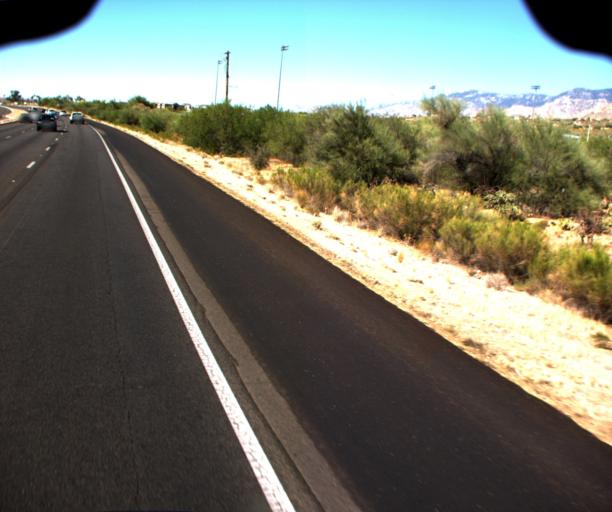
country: US
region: Arizona
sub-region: Pima County
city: Oro Valley
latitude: 32.3769
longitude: -110.9649
